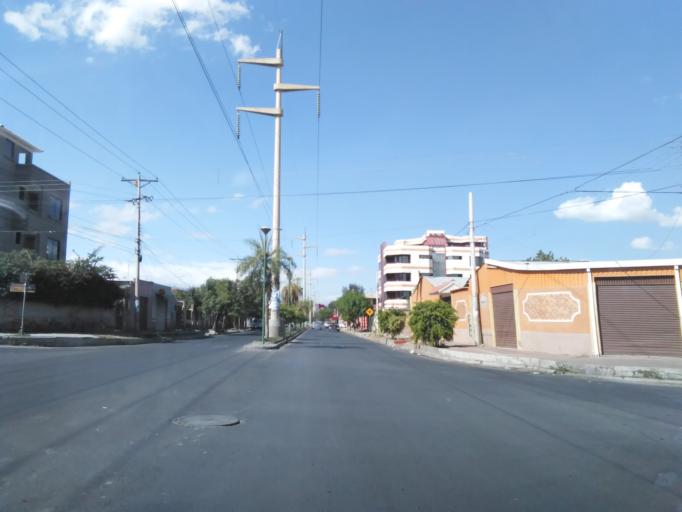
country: BO
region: Cochabamba
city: Cochabamba
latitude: -17.3964
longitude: -66.1754
